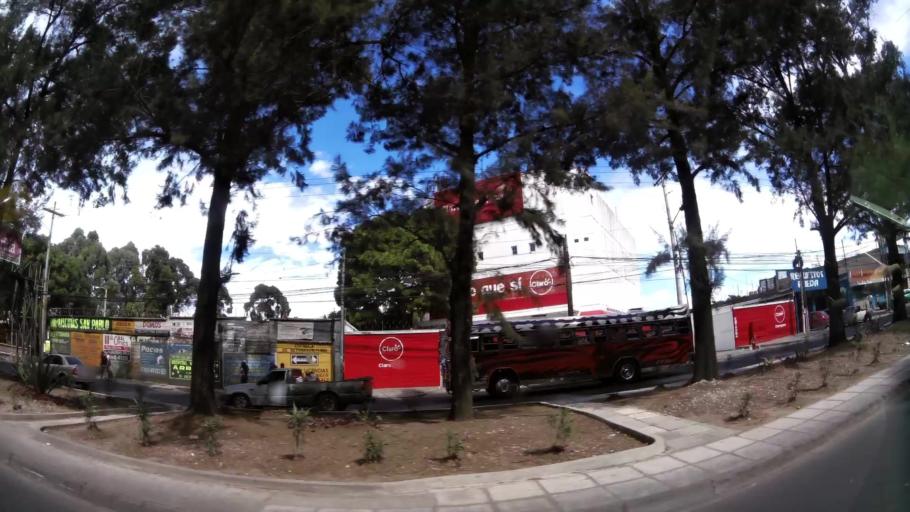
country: GT
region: Guatemala
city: Mixco
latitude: 14.6479
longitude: -90.5816
